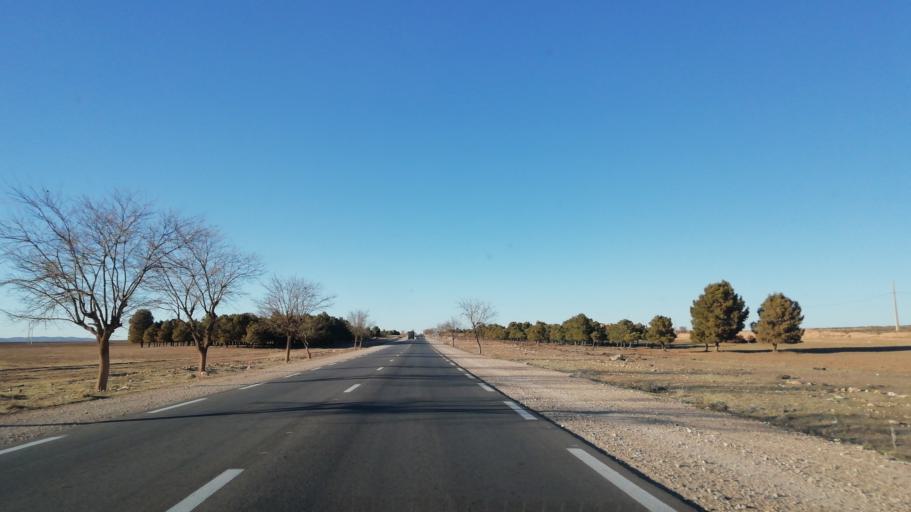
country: DZ
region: Tlemcen
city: Sebdou
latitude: 34.5239
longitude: -1.2910
